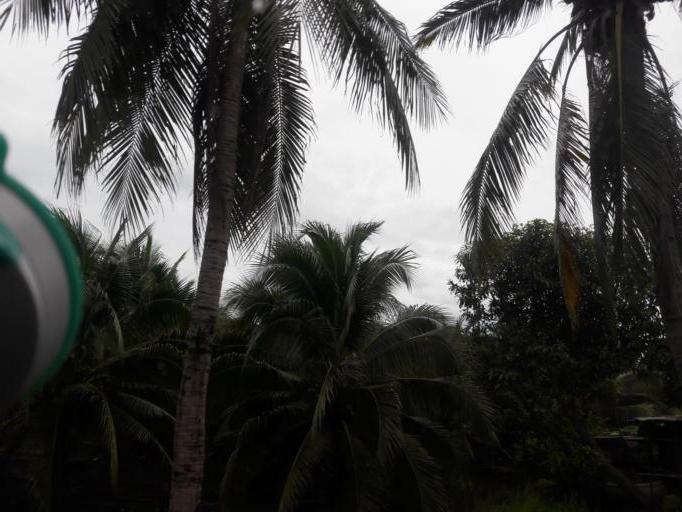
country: TH
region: Ratchaburi
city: Damnoen Saduak
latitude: 13.5190
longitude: 100.0192
